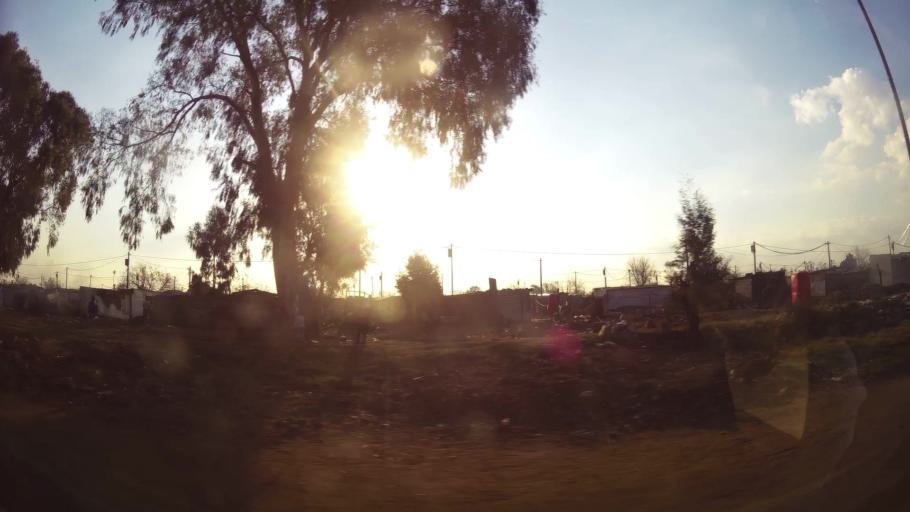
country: ZA
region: Gauteng
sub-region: Ekurhuleni Metropolitan Municipality
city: Boksburg
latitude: -26.3013
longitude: 28.2676
